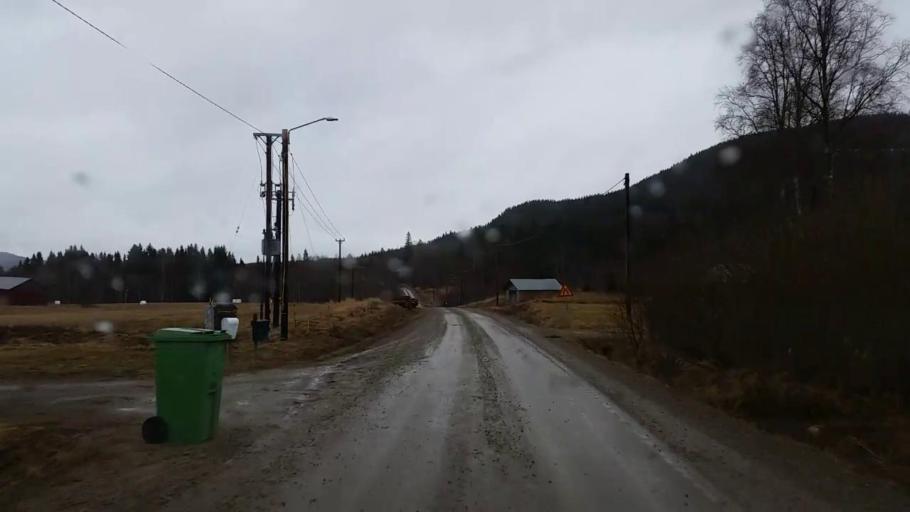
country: SE
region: Gaevleborg
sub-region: Ljusdals Kommun
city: Farila
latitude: 62.0669
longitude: 15.7833
